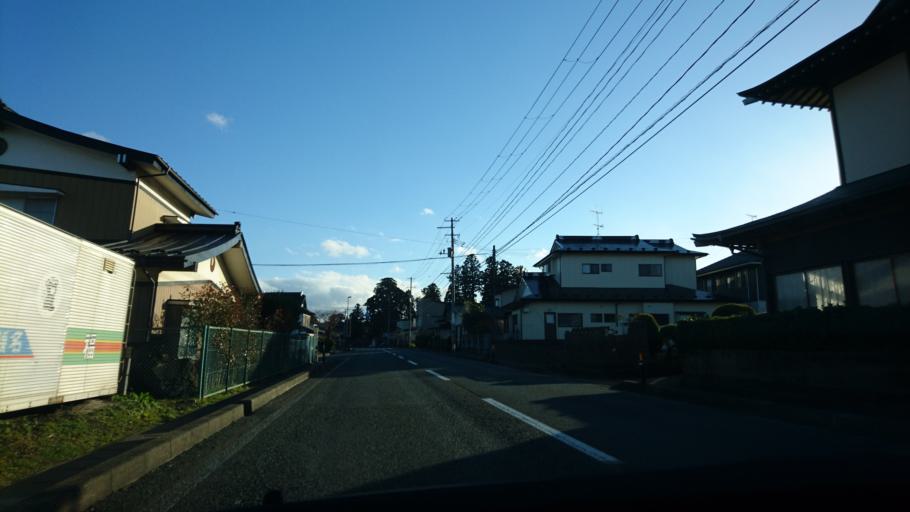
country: JP
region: Iwate
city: Ichinoseki
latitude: 38.9789
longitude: 141.1164
